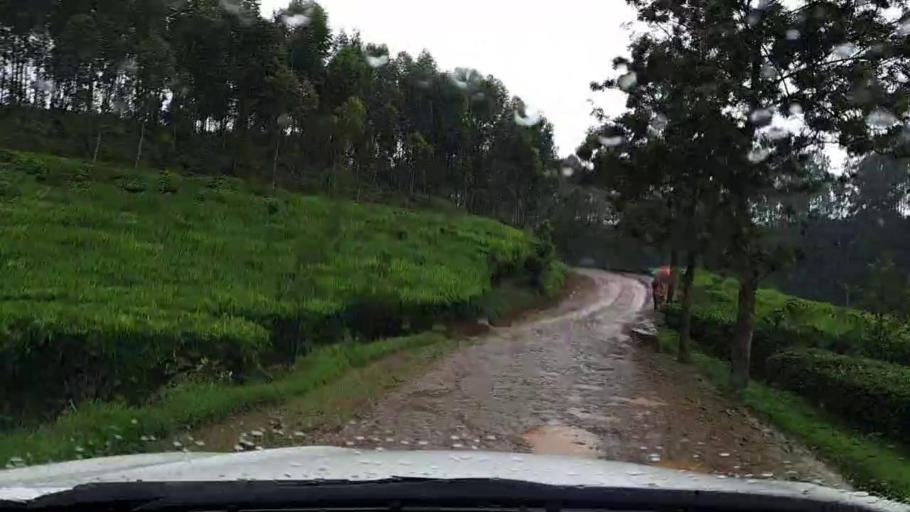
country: RW
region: Western Province
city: Cyangugu
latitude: -2.4509
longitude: 29.0393
